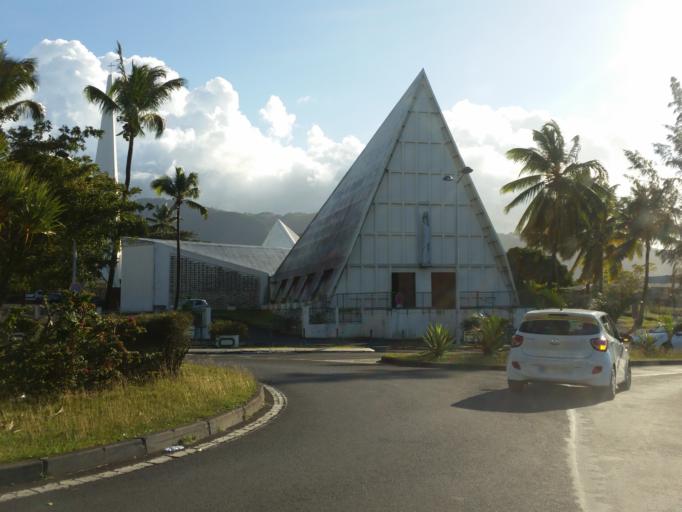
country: RE
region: Reunion
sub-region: Reunion
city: Saint-Denis
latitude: -20.8949
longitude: 55.4681
